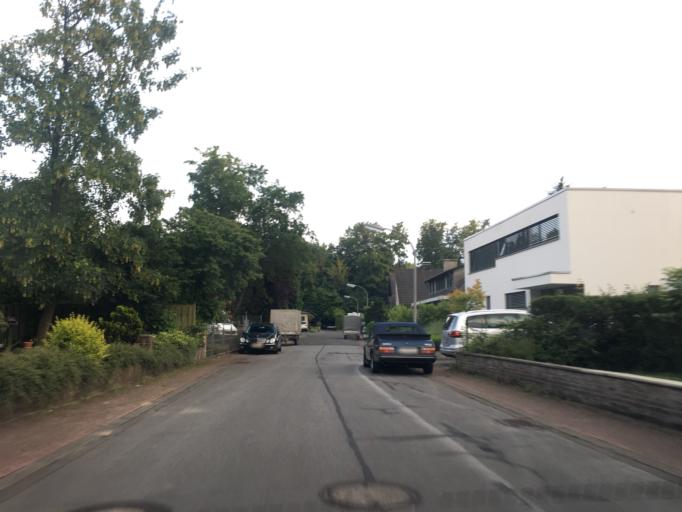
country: DE
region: North Rhine-Westphalia
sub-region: Regierungsbezirk Munster
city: Muenster
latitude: 51.9177
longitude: 7.5765
